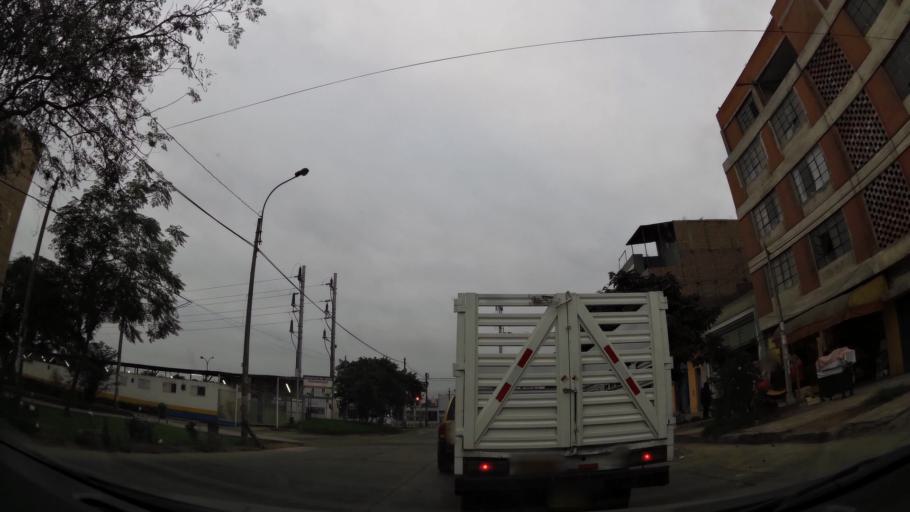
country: PE
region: Lima
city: Lima
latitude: -12.0494
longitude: -77.0672
